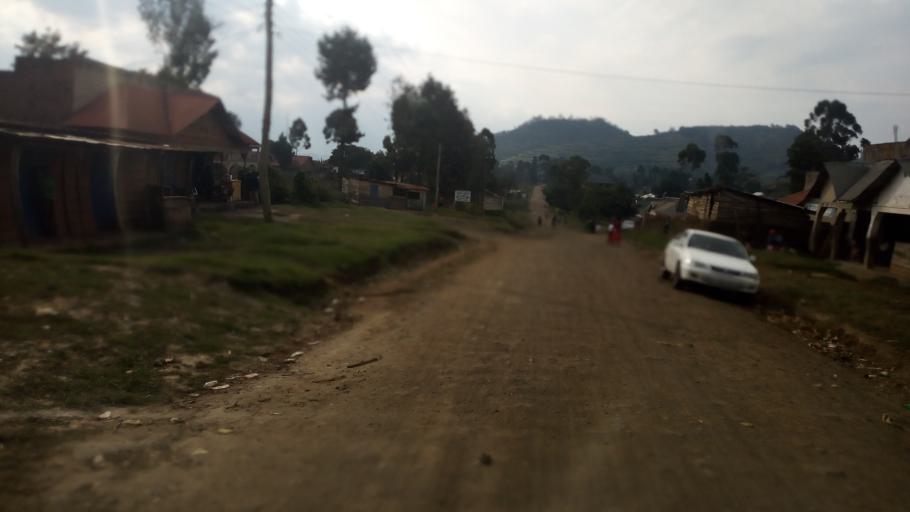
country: UG
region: Western Region
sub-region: Kisoro District
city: Kisoro
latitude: -1.2907
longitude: 29.6926
